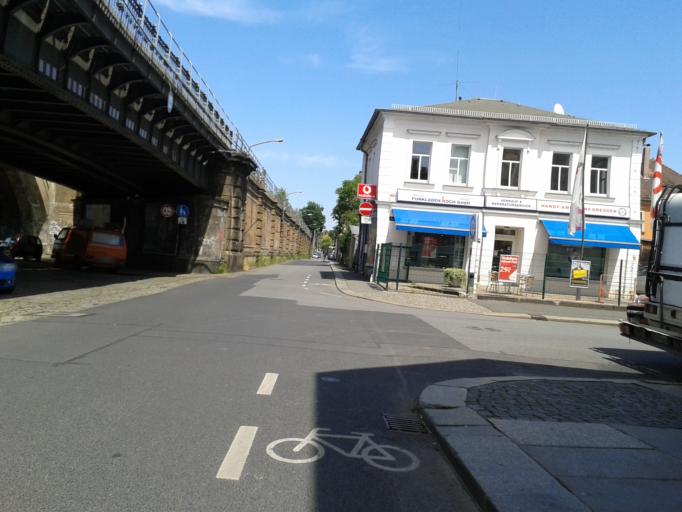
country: DE
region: Saxony
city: Dresden
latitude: 51.0703
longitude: 13.7473
